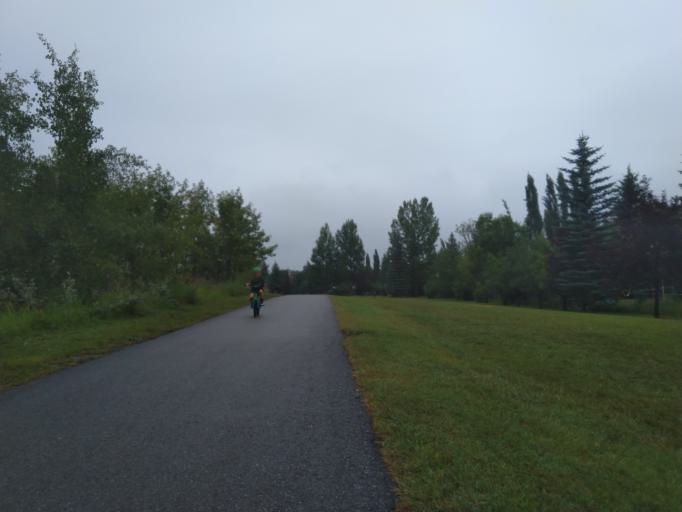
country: CA
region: Alberta
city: Cochrane
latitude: 51.1756
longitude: -114.4773
